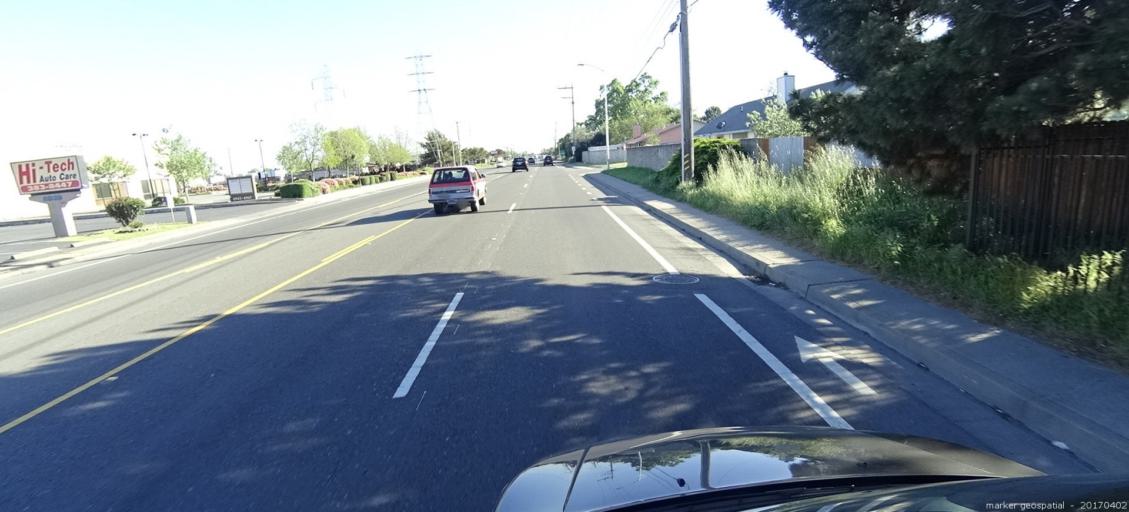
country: US
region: California
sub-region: Sacramento County
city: Florin
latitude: 38.5007
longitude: -121.4091
